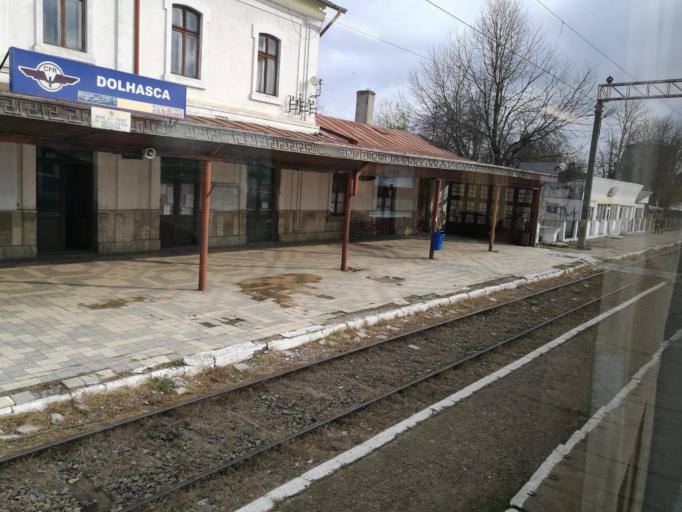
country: RO
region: Suceava
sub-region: Comuna Dolhasca
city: Dolhasca
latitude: 47.4270
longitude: 26.6084
